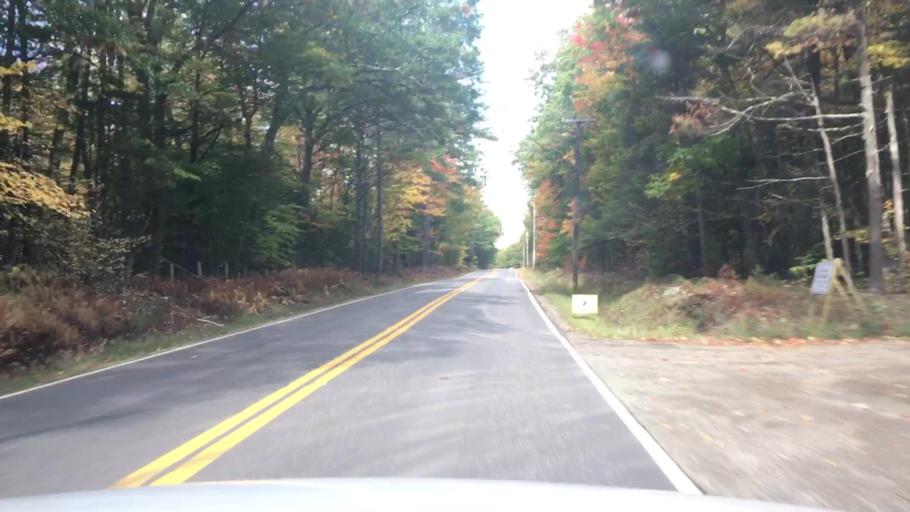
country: US
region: Maine
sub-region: Knox County
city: Hope
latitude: 44.2458
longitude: -69.1236
